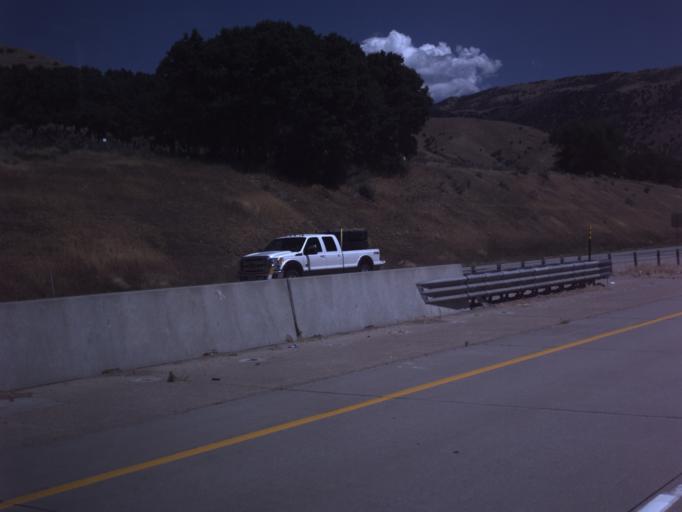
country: US
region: Utah
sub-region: Morgan County
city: Morgan
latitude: 41.0480
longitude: -111.6414
